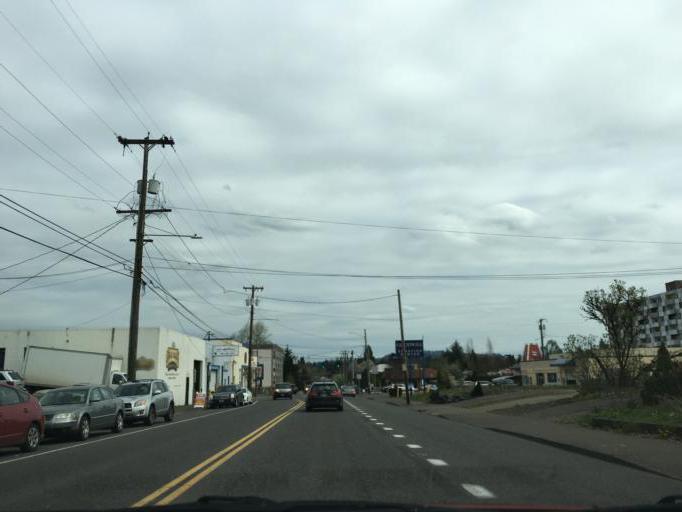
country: US
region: Oregon
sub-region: Clackamas County
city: Milwaukie
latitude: 45.4643
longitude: -122.6485
